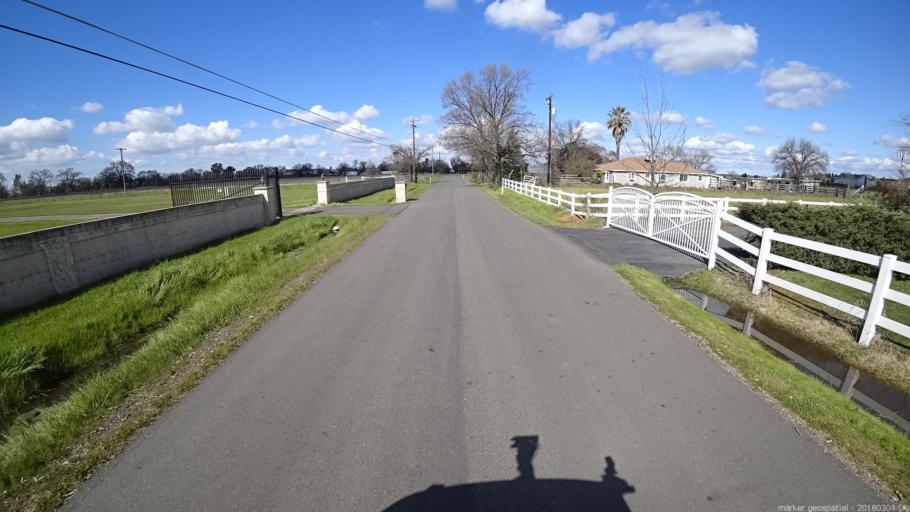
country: US
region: California
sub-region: Sacramento County
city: Vineyard
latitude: 38.4594
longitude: -121.3301
